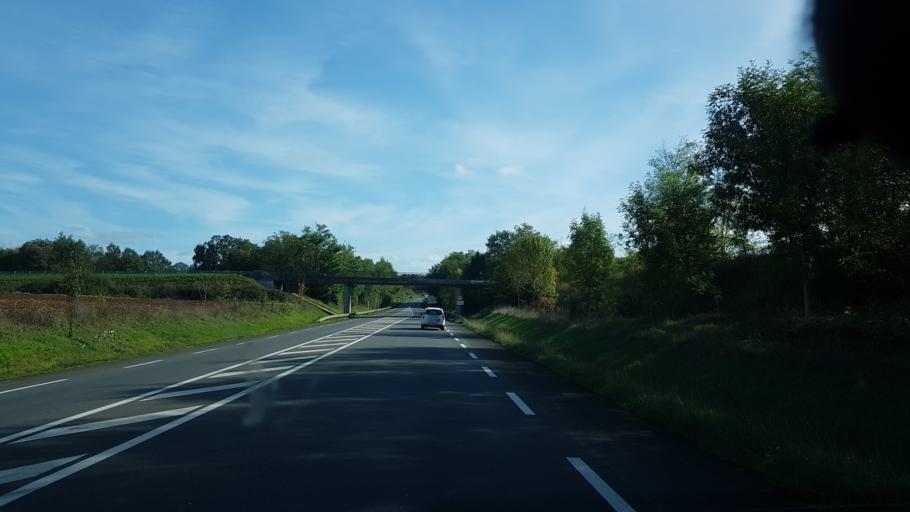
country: FR
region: Poitou-Charentes
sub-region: Departement de la Charente
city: Chasseneuil-sur-Bonnieure
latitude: 45.8362
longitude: 0.4650
